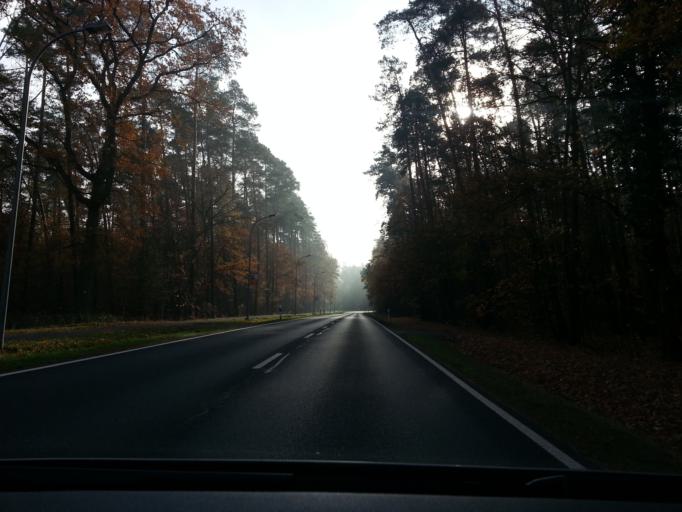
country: DE
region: Mecklenburg-Vorpommern
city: Torgelow
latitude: 53.6271
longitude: 14.0244
